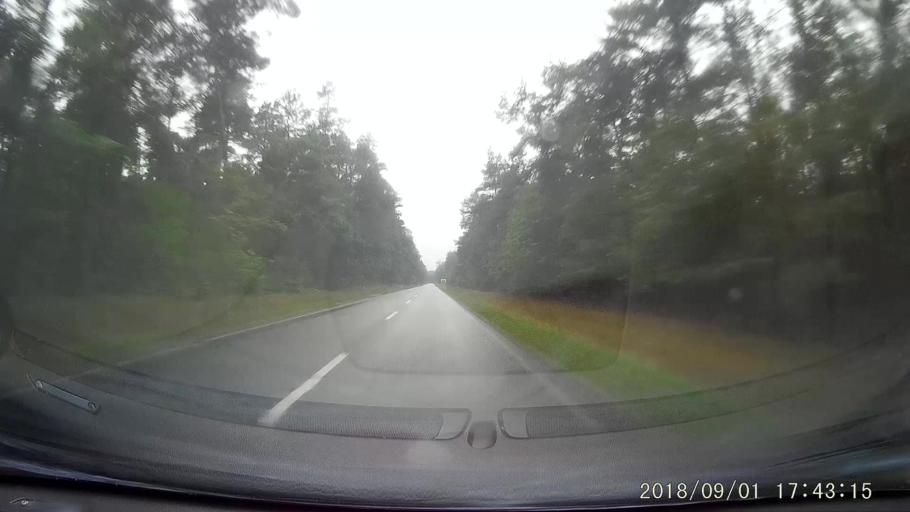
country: PL
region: Lubusz
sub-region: Powiat zaganski
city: Ilowa
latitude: 51.5464
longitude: 15.2517
